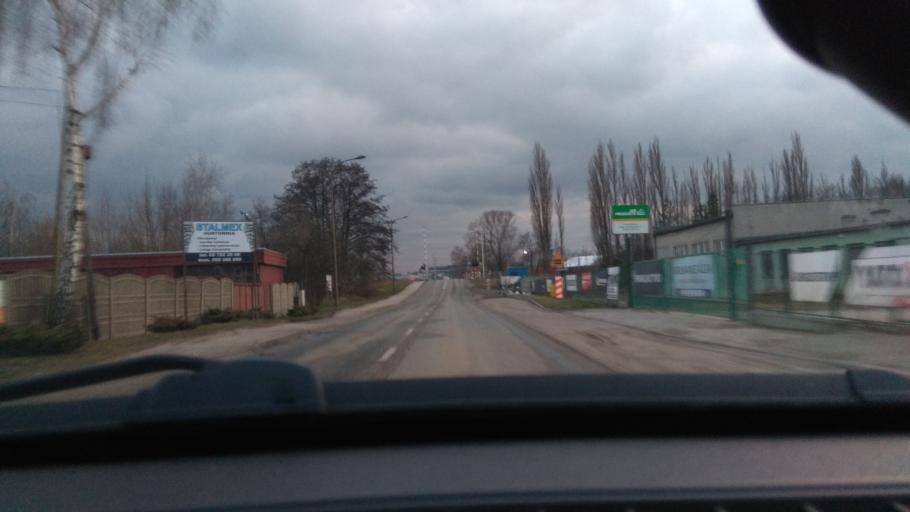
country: PL
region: Greater Poland Voivodeship
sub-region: Powiat kepinski
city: Kepno
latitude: 51.2950
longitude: 18.0061
